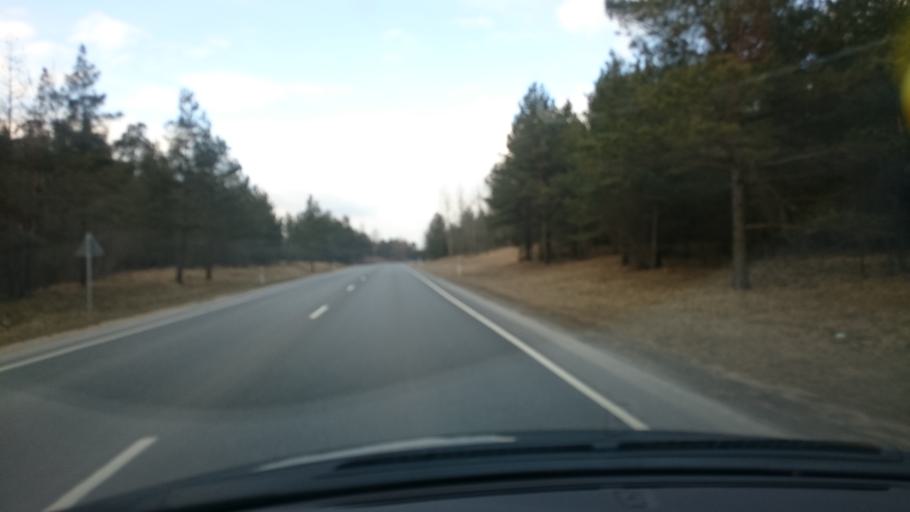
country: EE
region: Harju
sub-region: Nissi vald
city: Turba
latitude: 59.1021
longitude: 24.2529
